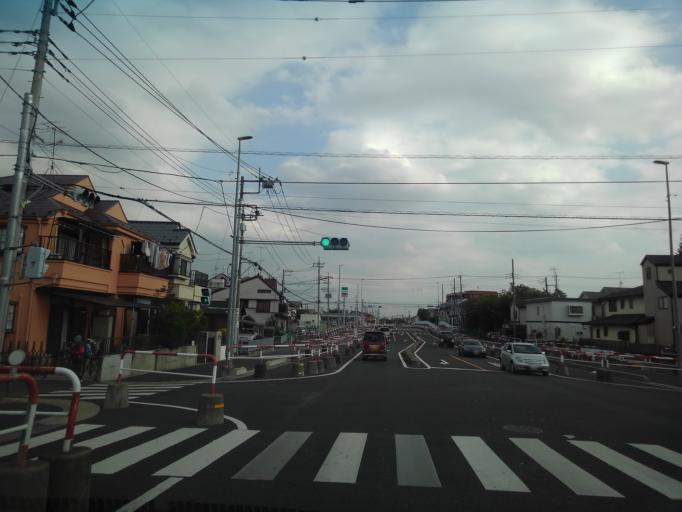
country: JP
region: Saitama
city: Tokorozawa
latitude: 35.7823
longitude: 139.4557
